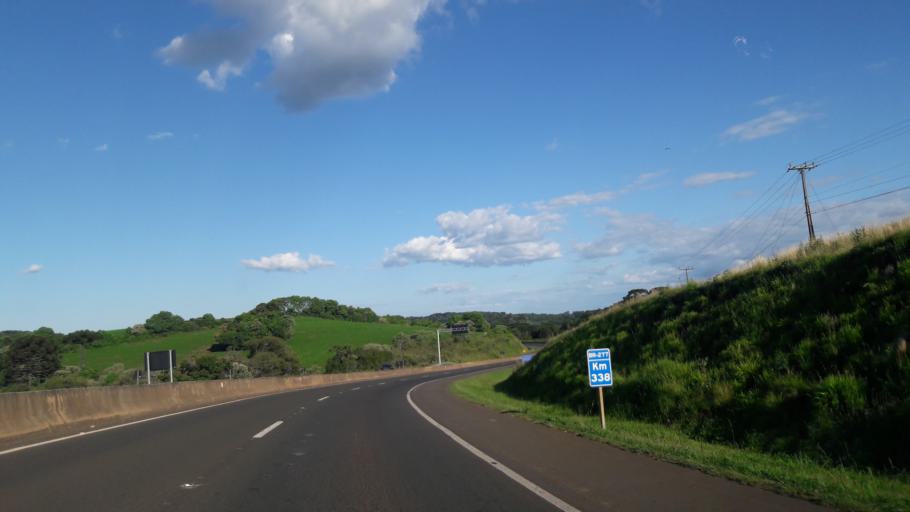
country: BR
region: Parana
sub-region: Guarapuava
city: Guarapuava
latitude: -25.3391
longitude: -51.4276
